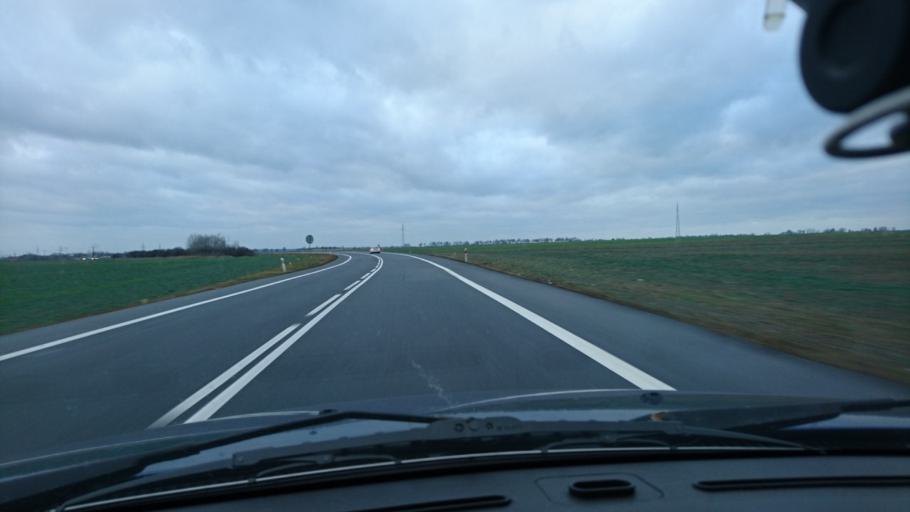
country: PL
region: Opole Voivodeship
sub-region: Powiat kluczborski
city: Kluczbork
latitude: 50.9875
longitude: 18.2367
